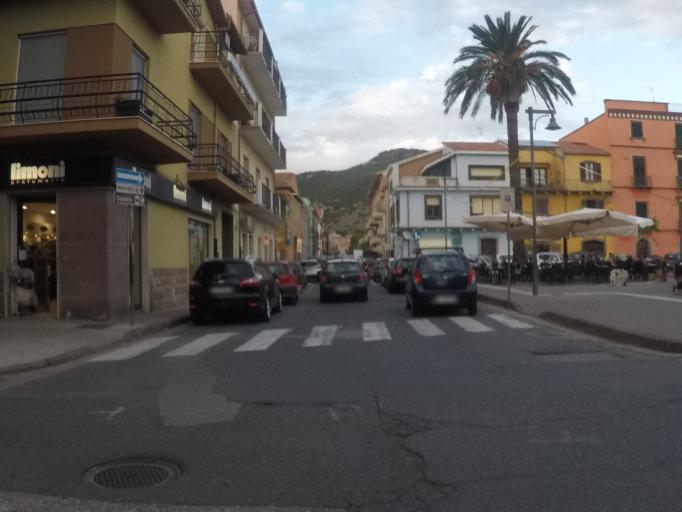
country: IT
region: Sardinia
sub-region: Provincia di Oristano
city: Bosa
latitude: 40.2964
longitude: 8.4992
